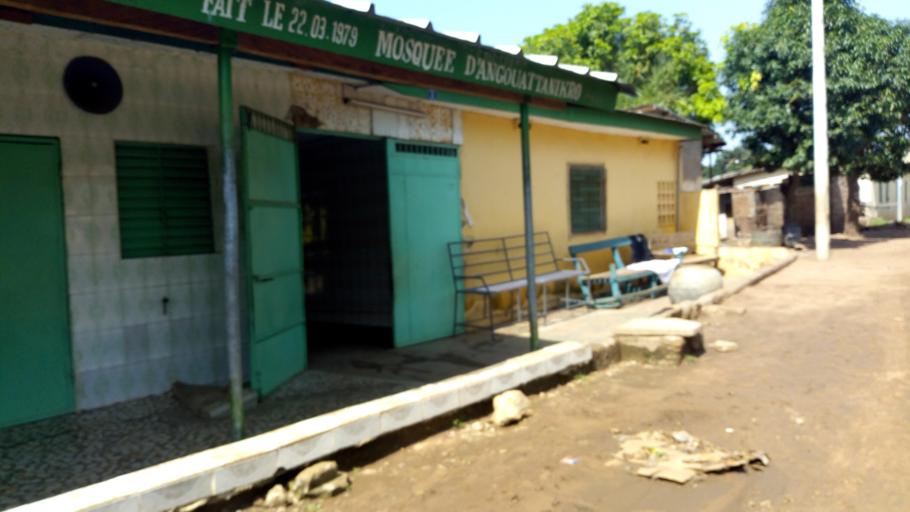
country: CI
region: Vallee du Bandama
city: Bouake
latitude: 7.6871
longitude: -5.0186
